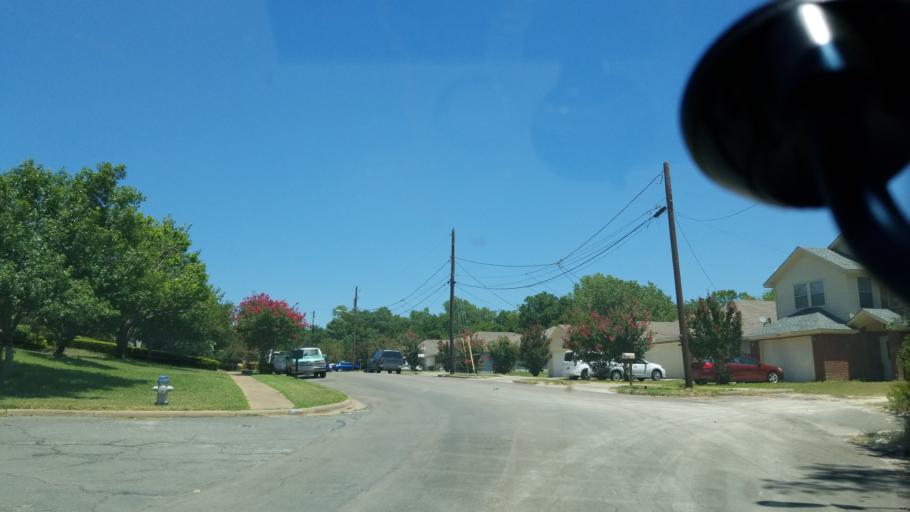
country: US
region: Texas
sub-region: Dallas County
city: Cockrell Hill
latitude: 32.6963
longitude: -96.8316
